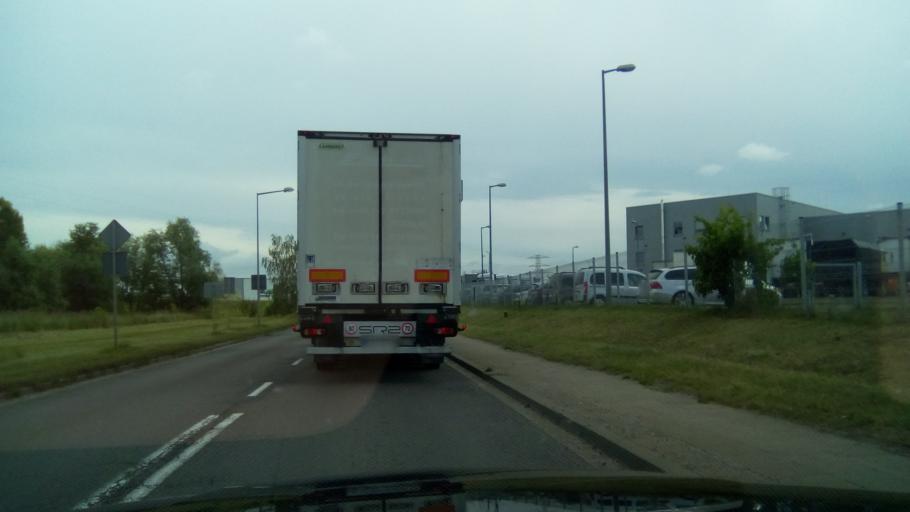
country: PL
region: Greater Poland Voivodeship
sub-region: Powiat poznanski
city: Komorniki
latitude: 52.3494
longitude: 16.8219
